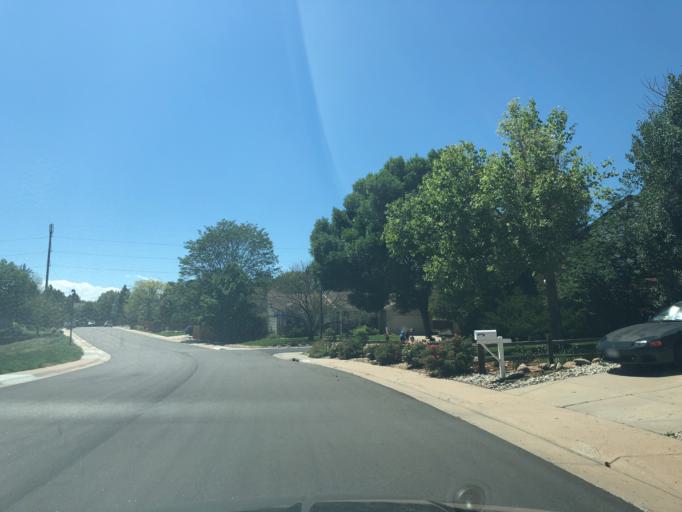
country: US
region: Colorado
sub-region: Arapahoe County
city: Dove Valley
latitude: 39.6156
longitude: -104.7891
